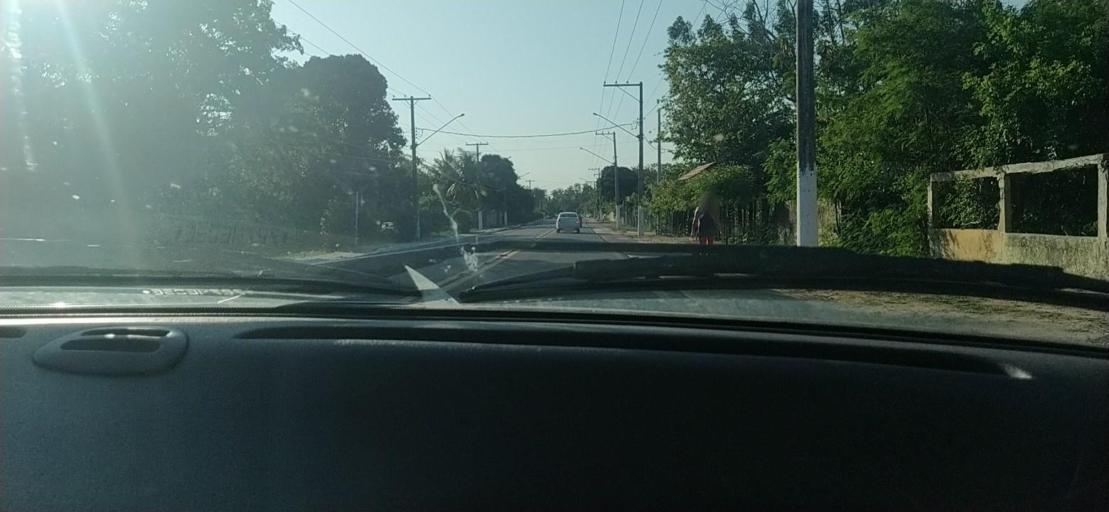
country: BR
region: Espirito Santo
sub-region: Conceicao Da Barra
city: Conceicao da Barra
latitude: -18.5696
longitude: -39.7407
